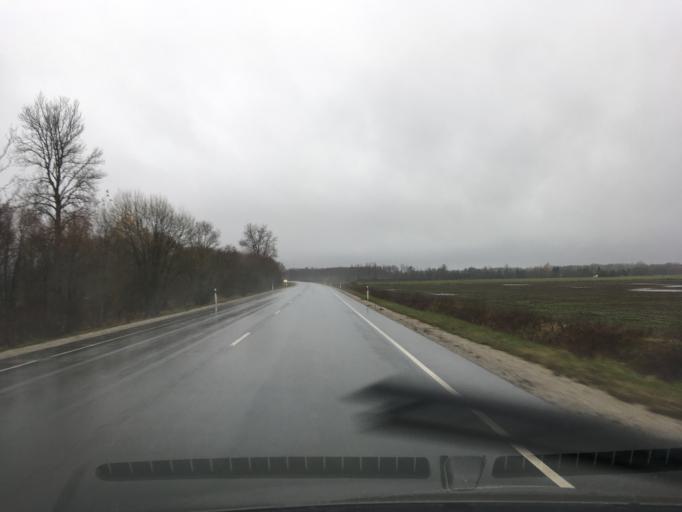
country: EE
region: Harju
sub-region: Nissi vald
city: Turba
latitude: 58.8654
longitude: 24.0779
